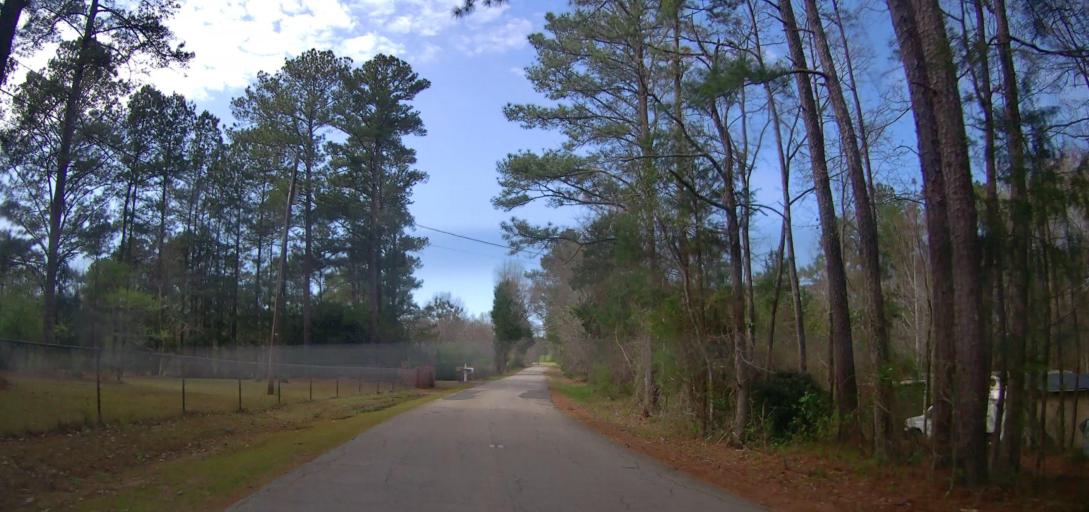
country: US
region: Georgia
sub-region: Monroe County
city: Forsyth
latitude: 33.0434
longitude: -83.8981
